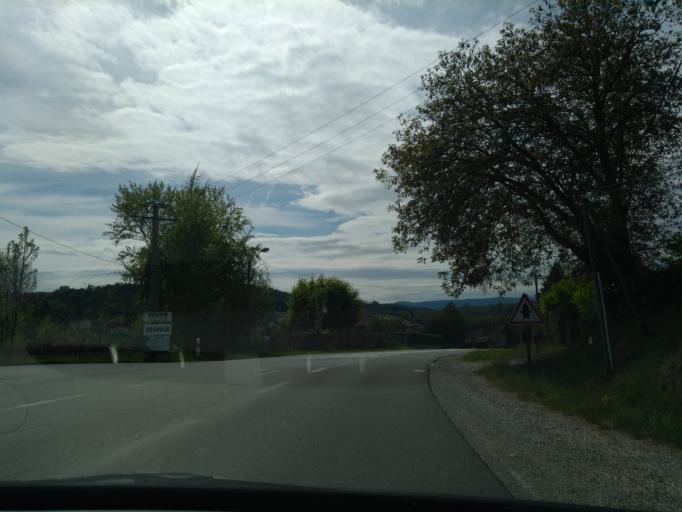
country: FR
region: Rhone-Alpes
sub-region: Departement de la Haute-Savoie
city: Chavanod
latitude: 45.8796
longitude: 6.0421
